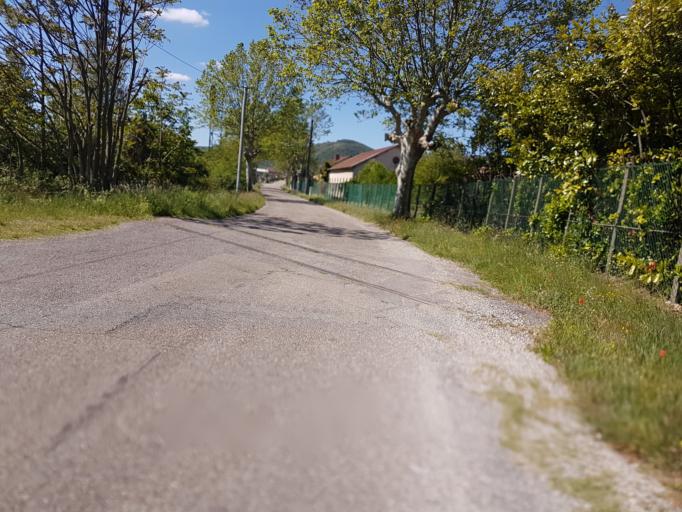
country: FR
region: Rhone-Alpes
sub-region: Departement de la Drome
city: Andancette
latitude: 45.2498
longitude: 4.8097
